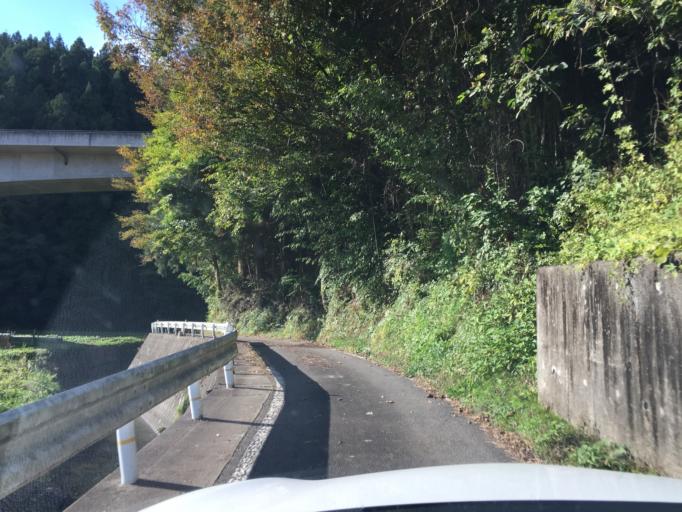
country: JP
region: Fukushima
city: Ishikawa
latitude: 37.1603
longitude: 140.5112
